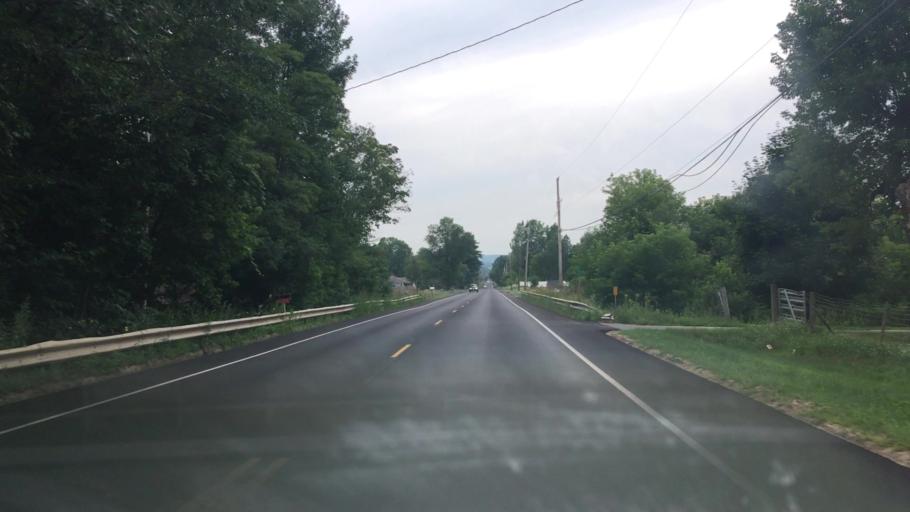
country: US
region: New York
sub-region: Clinton County
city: Plattsburgh West
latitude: 44.6526
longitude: -73.5146
